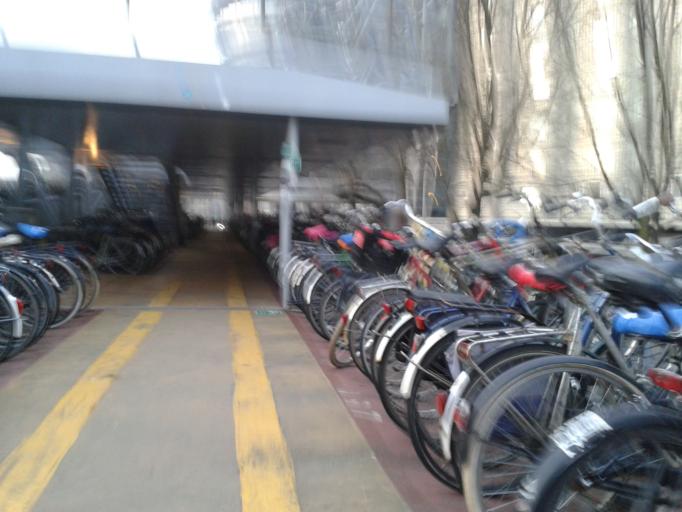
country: NL
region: North Holland
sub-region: Gemeente Amsterdam
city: Amsterdam
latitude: 52.3793
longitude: 4.8971
